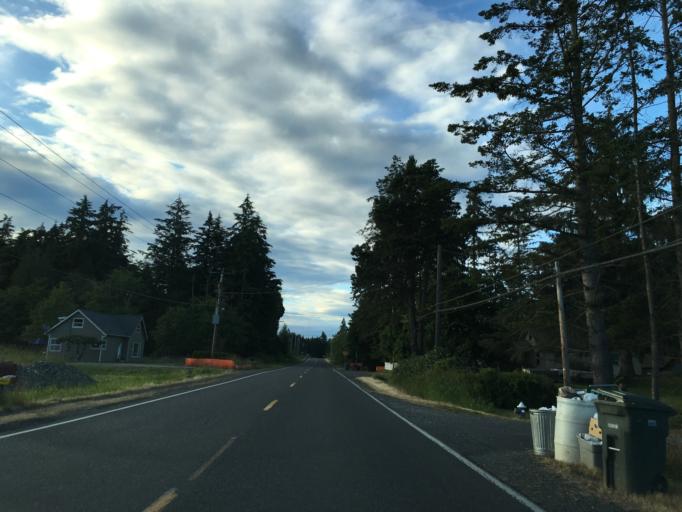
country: US
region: Washington
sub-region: Whatcom County
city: Blaine
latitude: 48.9661
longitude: -122.7299
